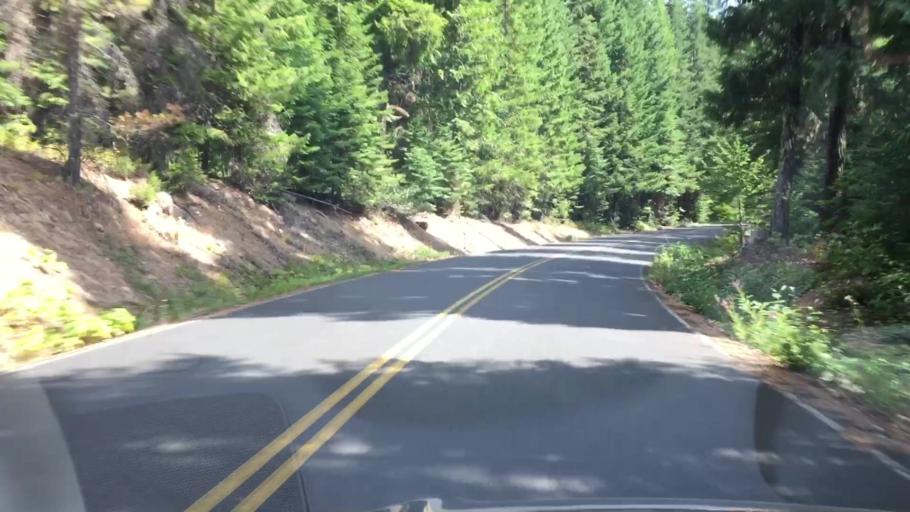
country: US
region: Washington
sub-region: Klickitat County
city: White Salmon
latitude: 46.0816
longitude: -121.5923
